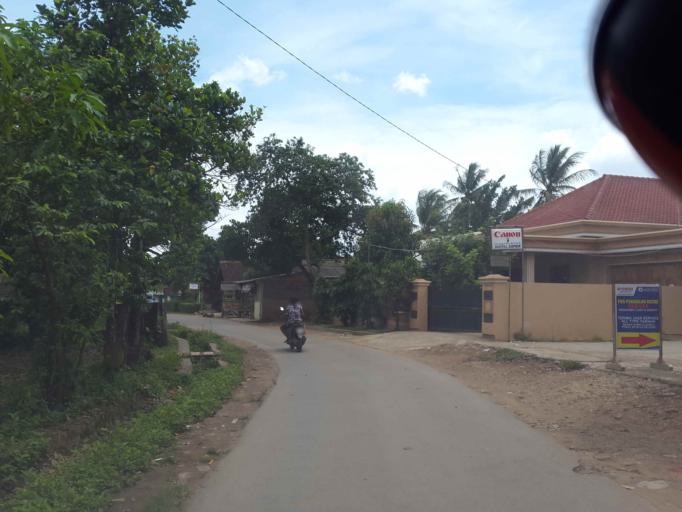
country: ID
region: Lampung
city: Natar
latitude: -5.3144
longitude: 105.2067
